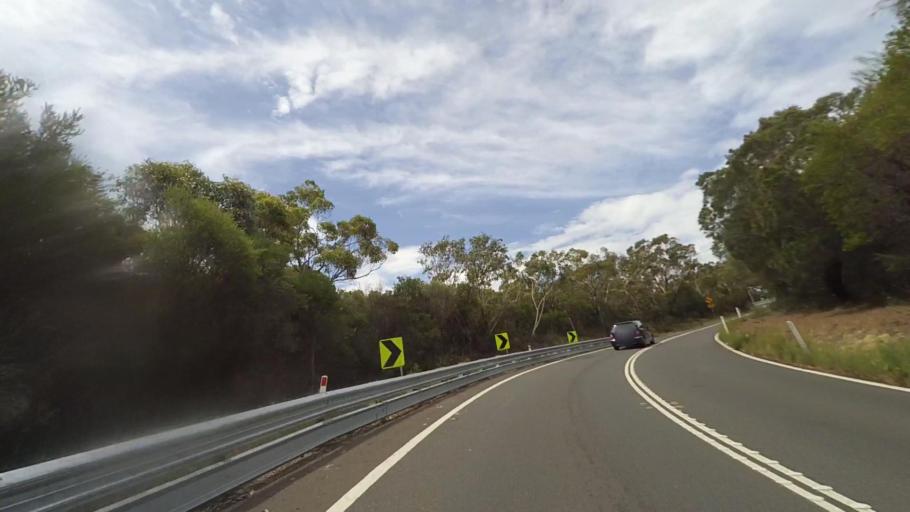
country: AU
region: New South Wales
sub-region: Sutherland Shire
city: Loftus
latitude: -34.0650
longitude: 151.0559
